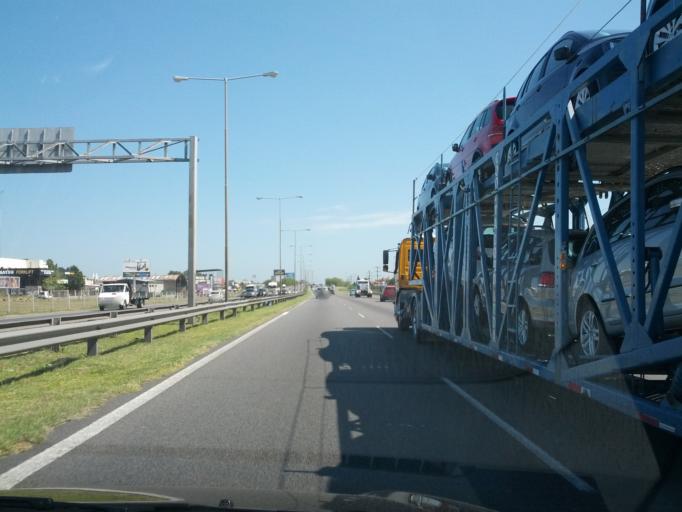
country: AR
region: Buenos Aires
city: Santa Catalina - Dique Lujan
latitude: -34.4136
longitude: -58.7255
